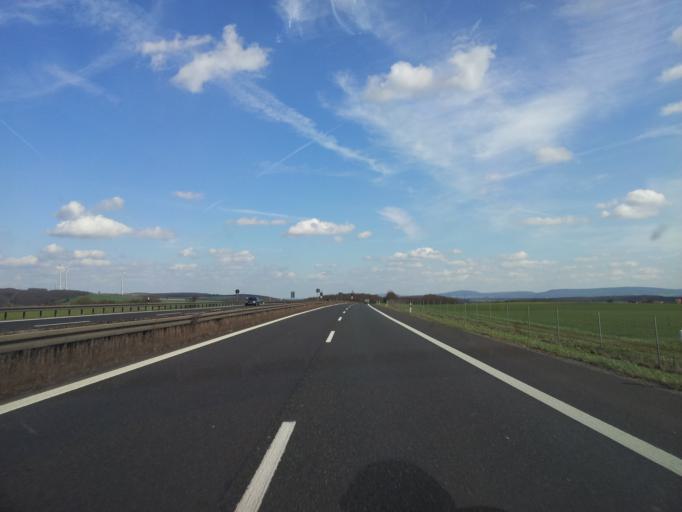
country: DE
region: Bavaria
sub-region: Regierungsbezirk Unterfranken
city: Gochsheim
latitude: 50.0290
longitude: 10.3008
